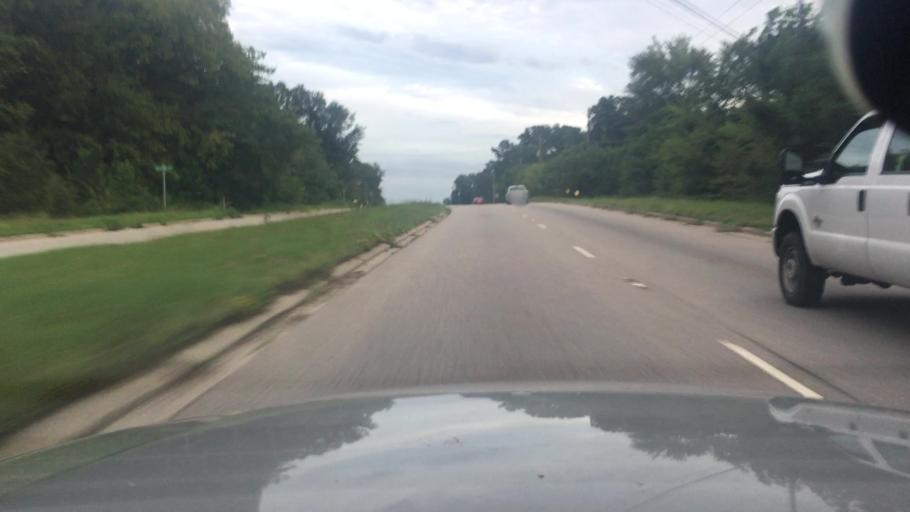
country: US
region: North Carolina
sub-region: Cumberland County
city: Hope Mills
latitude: 34.9999
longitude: -78.9740
